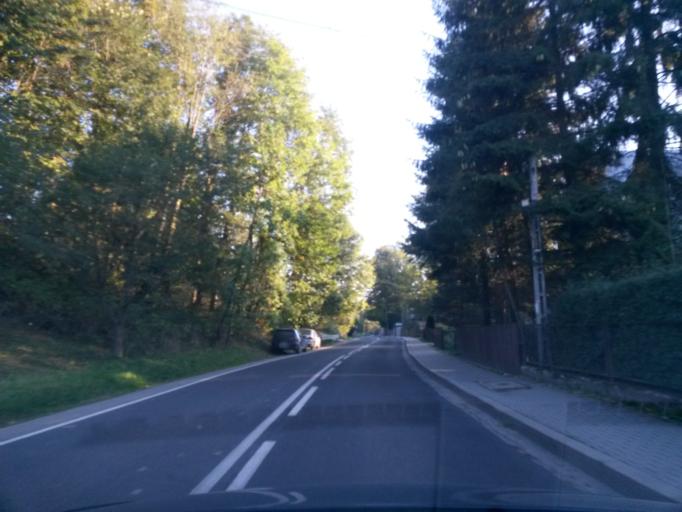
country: PL
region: Lesser Poland Voivodeship
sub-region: Powiat nowotarski
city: Czarny Dunajec
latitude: 49.3650
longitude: 19.8182
